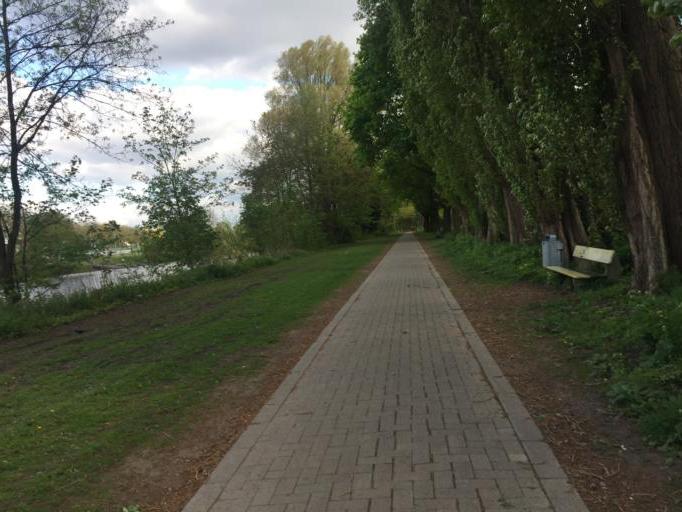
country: DE
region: North Rhine-Westphalia
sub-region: Regierungsbezirk Munster
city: Rheine
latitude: 52.2765
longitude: 7.4442
